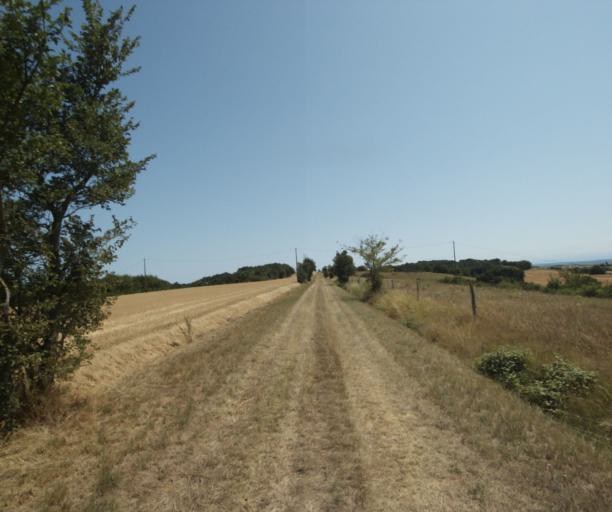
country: FR
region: Midi-Pyrenees
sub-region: Departement de la Haute-Garonne
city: Saint-Felix-Lauragais
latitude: 43.4453
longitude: 1.8634
